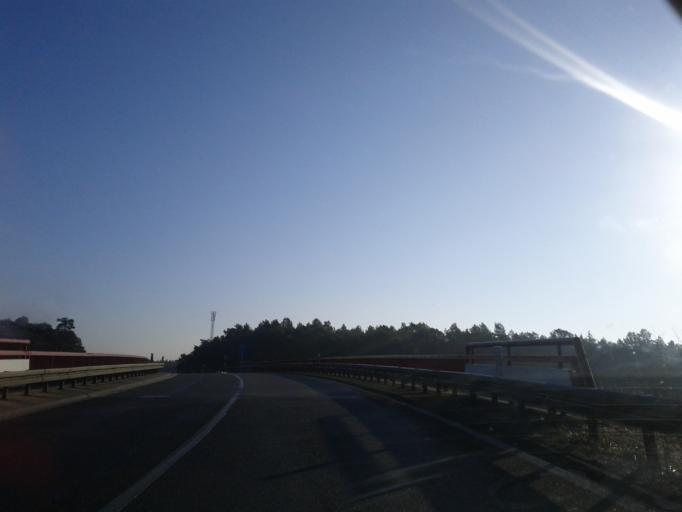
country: DE
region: Brandenburg
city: Erkner
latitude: 52.3887
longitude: 13.7857
